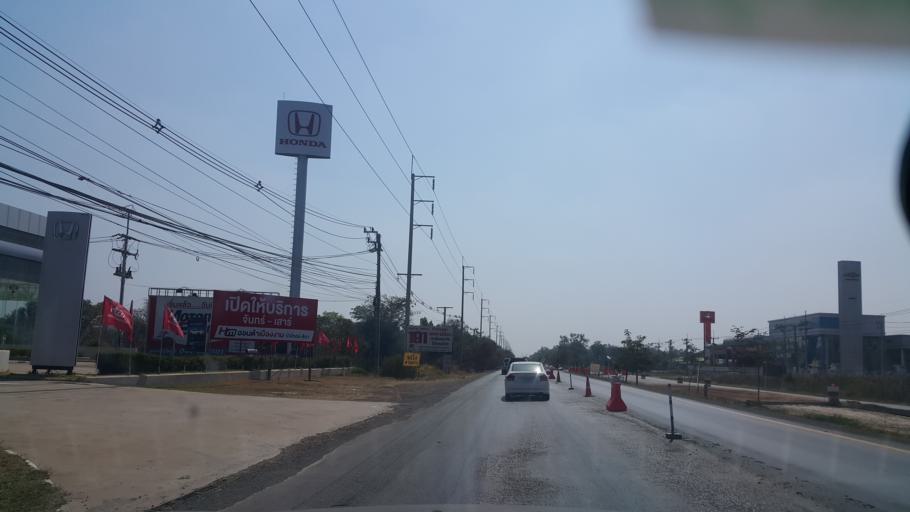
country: TH
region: Nakhon Ratchasima
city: Sida
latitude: 15.5708
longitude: 102.5539
